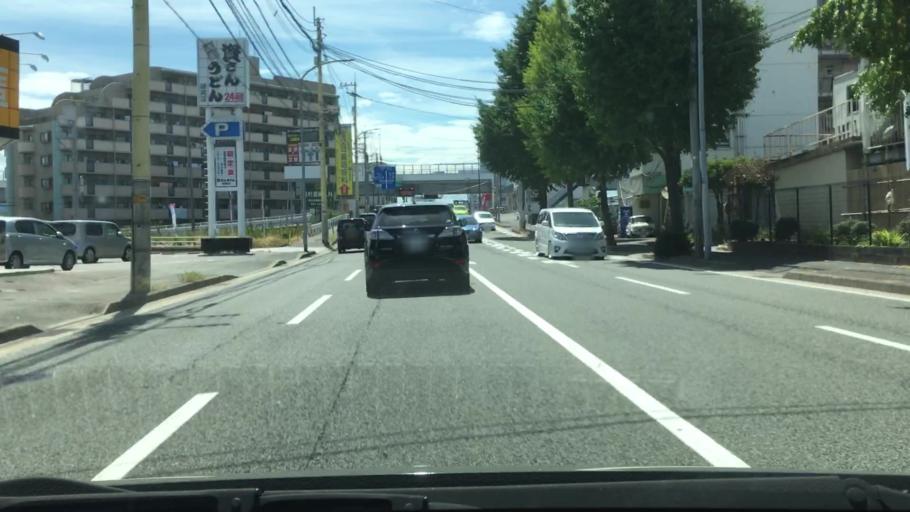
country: JP
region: Fukuoka
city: Onojo
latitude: 33.5567
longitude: 130.4522
